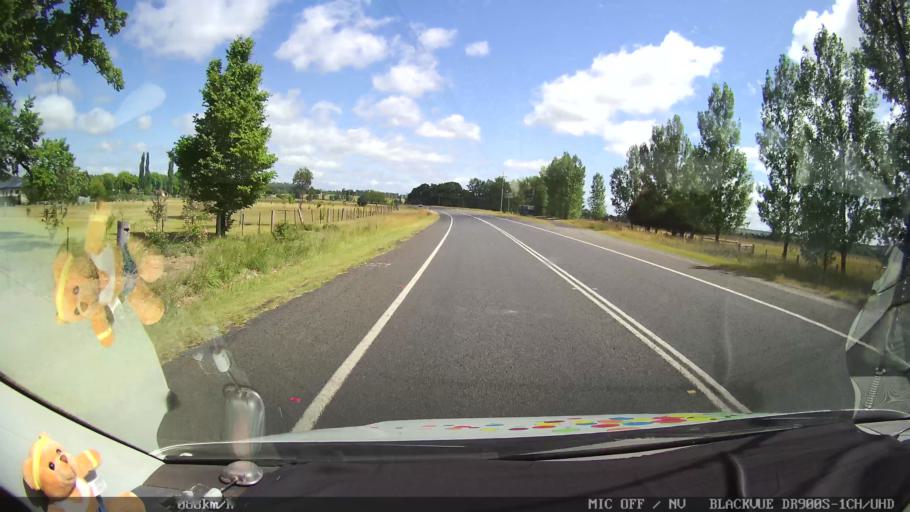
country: AU
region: New South Wales
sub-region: Glen Innes Severn
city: Glen Innes
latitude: -29.8134
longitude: 151.7413
